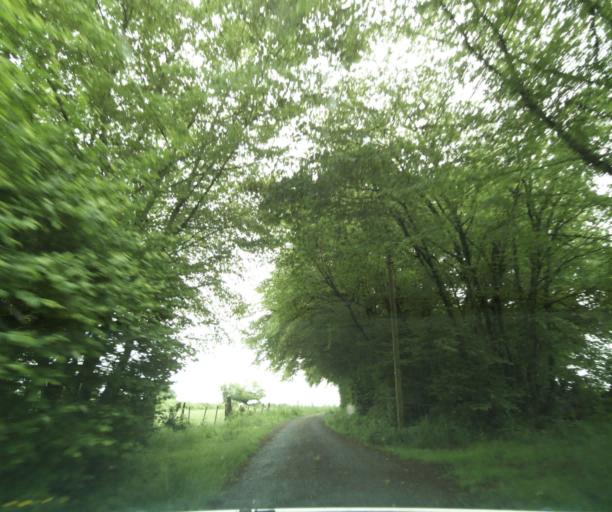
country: FR
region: Bourgogne
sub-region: Departement de Saone-et-Loire
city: Charolles
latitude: 46.4648
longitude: 4.3341
